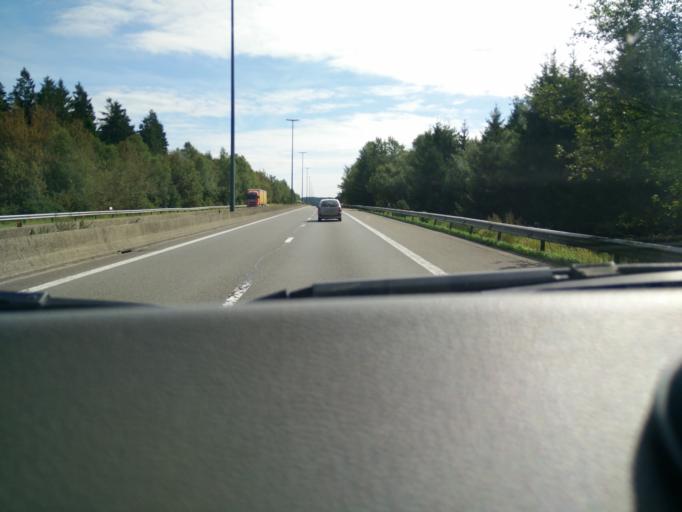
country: BE
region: Wallonia
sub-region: Province du Luxembourg
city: Bertrix
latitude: 49.9107
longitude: 5.2776
